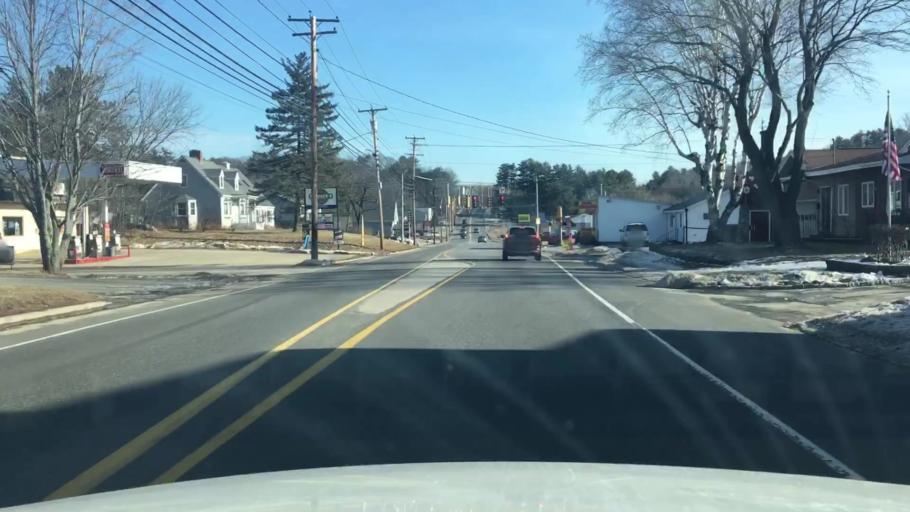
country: US
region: Maine
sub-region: Androscoggin County
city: Sabattus
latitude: 44.1007
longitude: -70.1552
